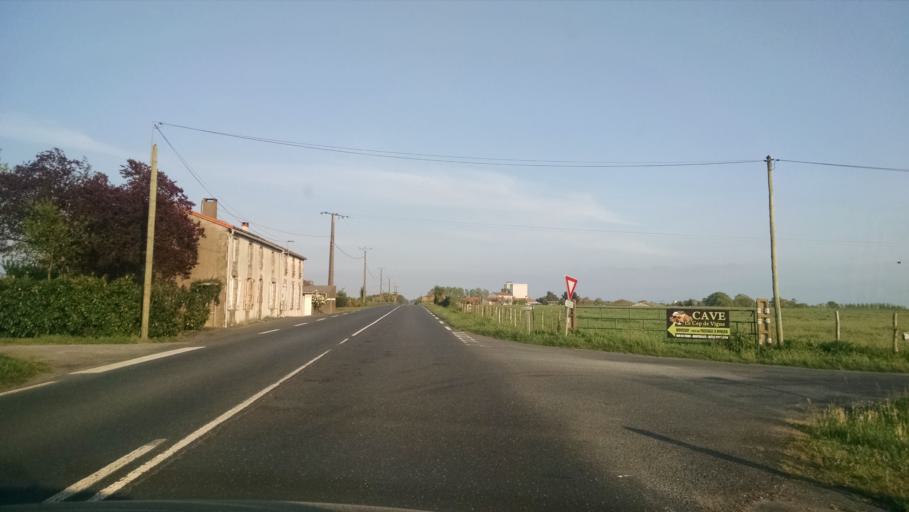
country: FR
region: Pays de la Loire
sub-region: Departement de la Loire-Atlantique
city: Boussay
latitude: 47.0638
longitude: -1.1964
